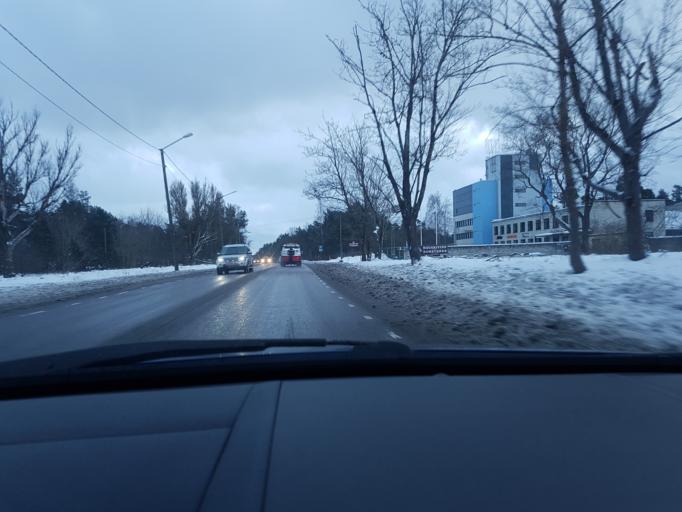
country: EE
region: Harju
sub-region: Tallinna linn
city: Tallinn
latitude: 59.3896
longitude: 24.7322
